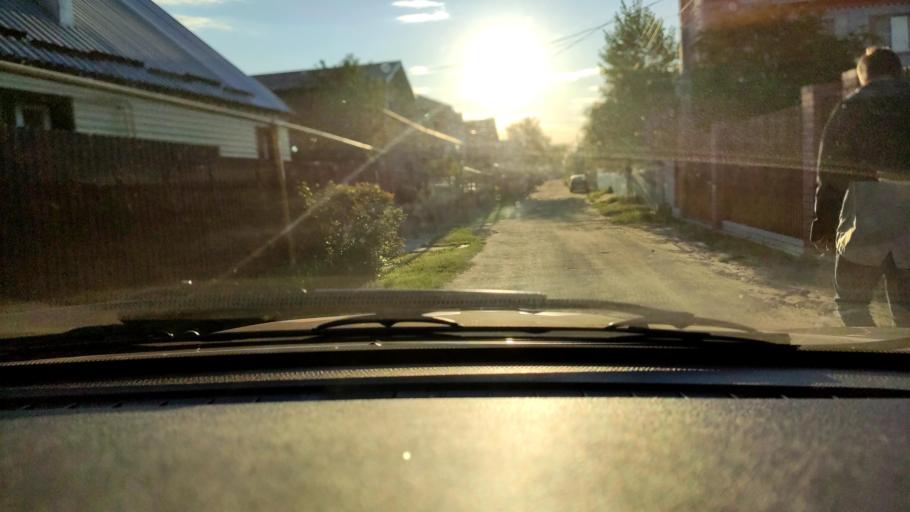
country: RU
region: Voronezj
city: Pridonskoy
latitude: 51.6391
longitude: 39.0868
